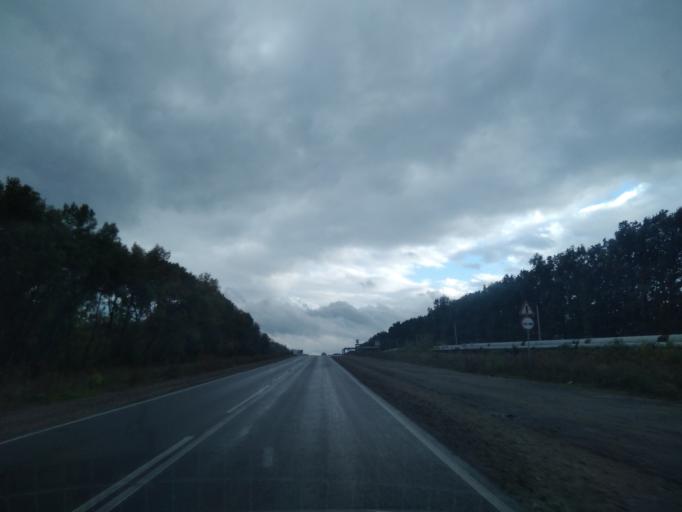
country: RU
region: Tula
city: Yefremov
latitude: 53.1119
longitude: 38.1416
